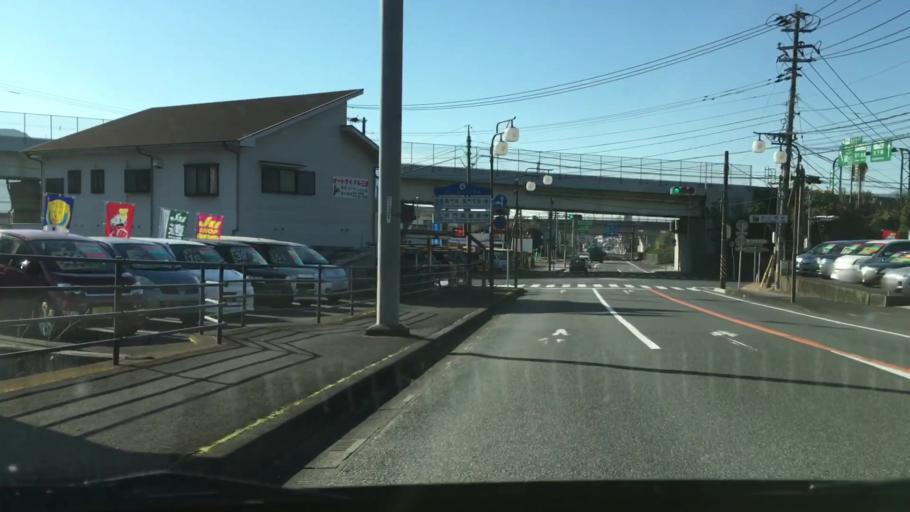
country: JP
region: Kagoshima
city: Kajiki
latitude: 31.7479
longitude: 130.6710
